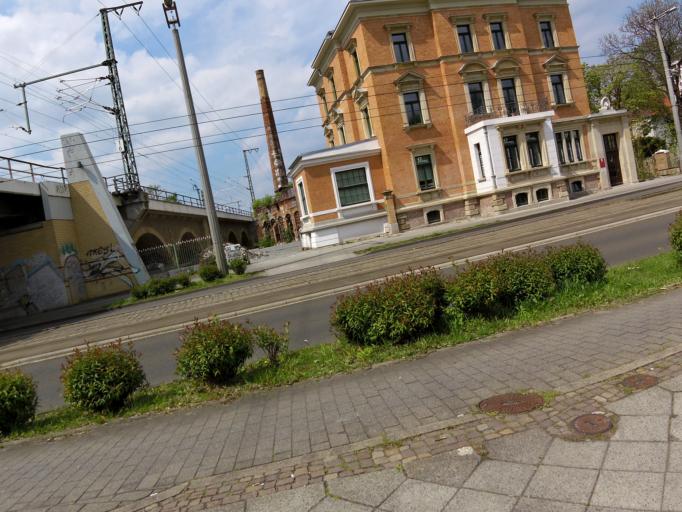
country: DE
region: Saxony
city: Leipzig
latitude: 51.3606
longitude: 12.3805
